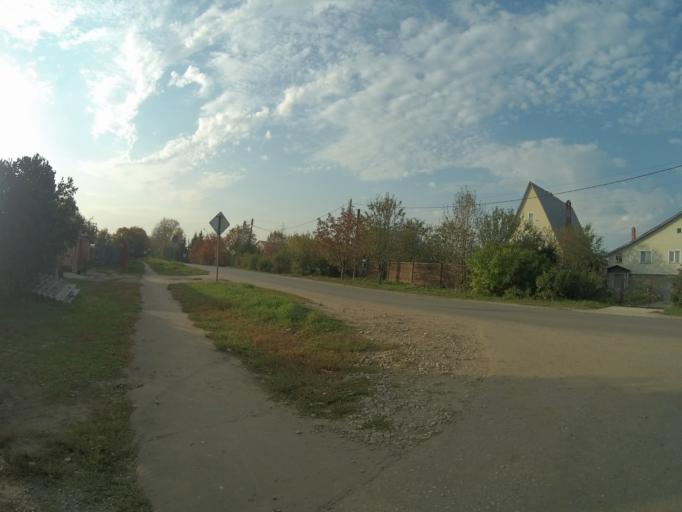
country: RU
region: Vladimir
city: Bogolyubovo
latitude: 56.1896
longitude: 40.5052
